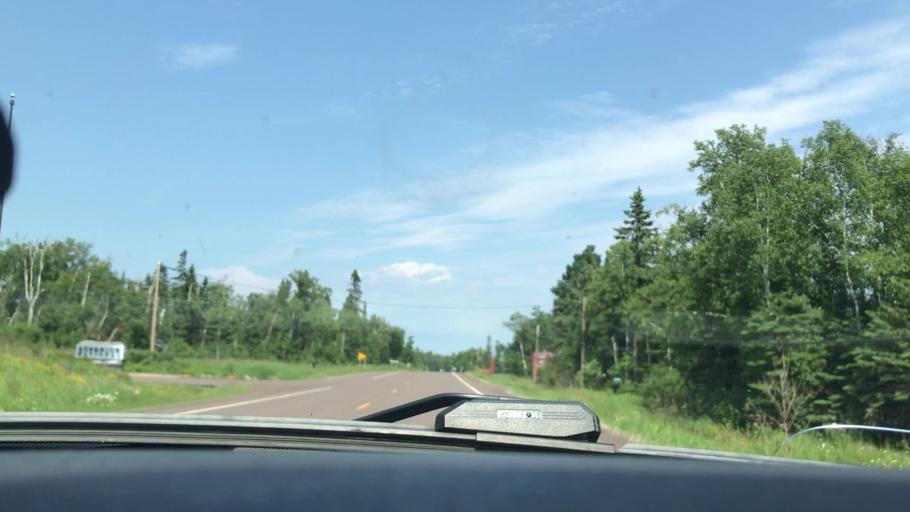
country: US
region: Minnesota
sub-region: Cook County
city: Grand Marais
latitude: 47.6364
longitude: -90.7134
